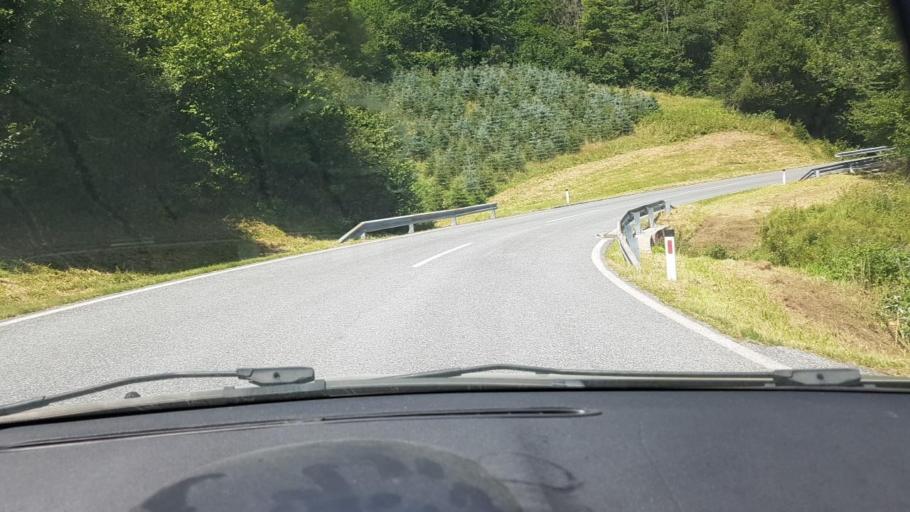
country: SI
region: Jezersko
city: Zgornje Jezersko
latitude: 46.4216
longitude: 14.5364
